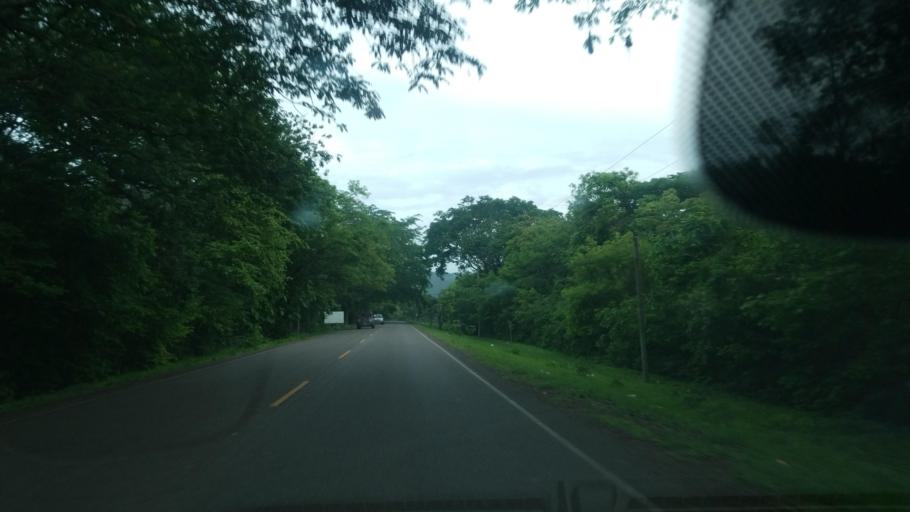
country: HN
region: Santa Barbara
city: San Vicente Centenario
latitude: 14.8760
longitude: -88.2483
